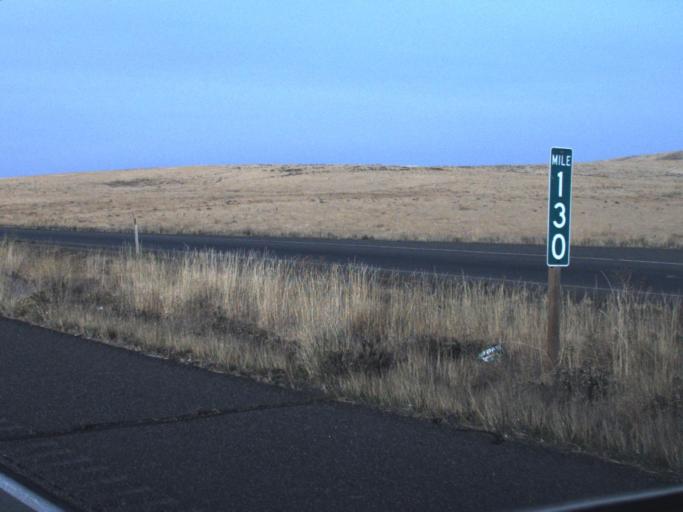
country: US
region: Oregon
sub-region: Umatilla County
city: Umatilla
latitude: 45.9627
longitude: -119.3423
